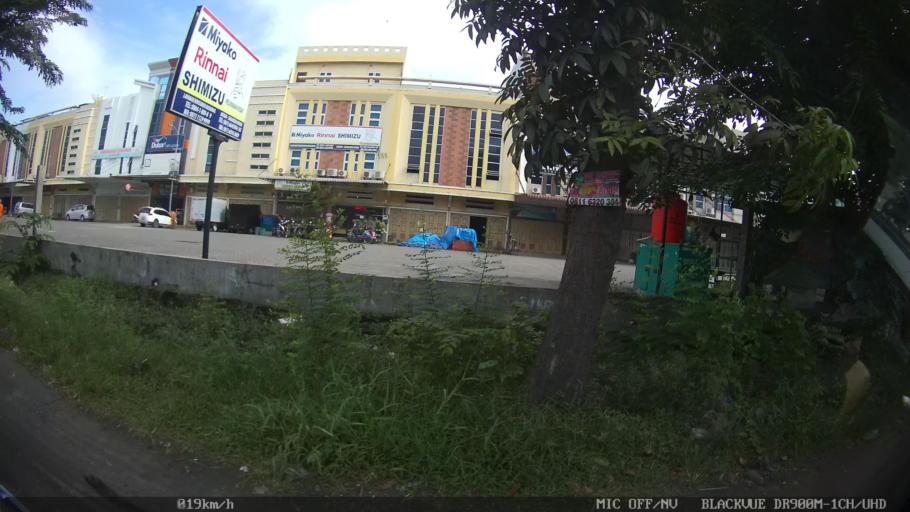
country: ID
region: North Sumatra
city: Medan
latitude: 3.6288
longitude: 98.7029
